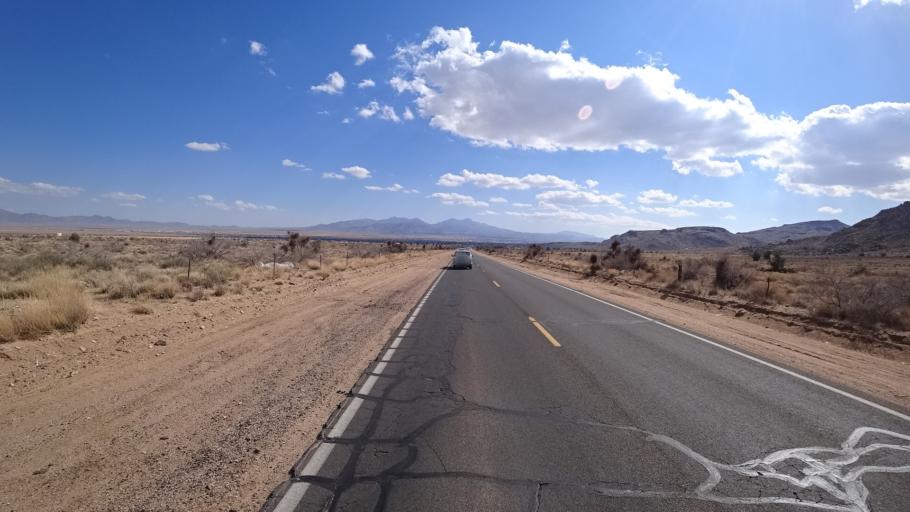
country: US
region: Arizona
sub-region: Mohave County
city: New Kingman-Butler
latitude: 35.2835
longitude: -114.0536
